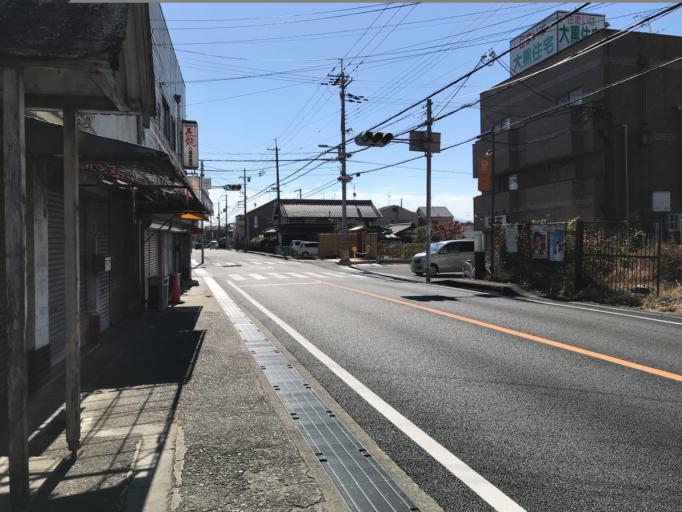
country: JP
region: Osaka
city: Kashihara
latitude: 34.5465
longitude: 135.6087
